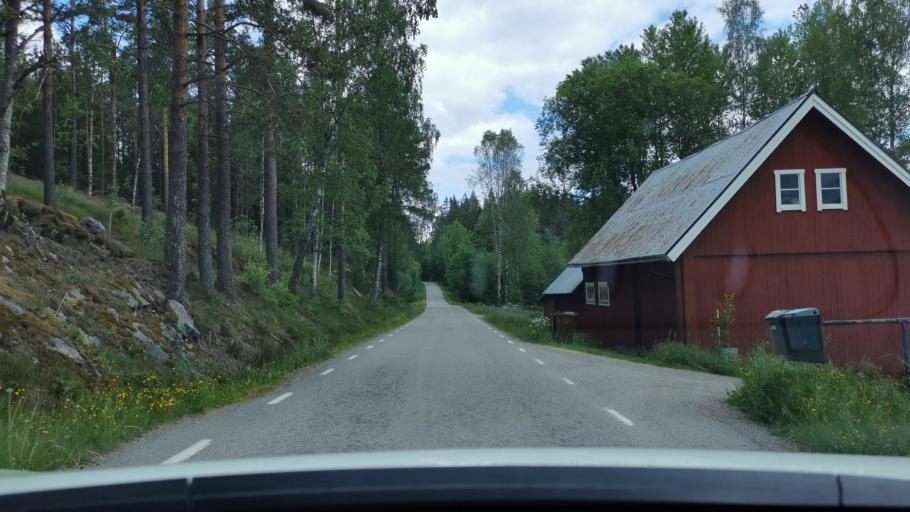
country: SE
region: Vaestra Goetaland
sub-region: Bengtsfors Kommun
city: Dals Langed
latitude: 58.8482
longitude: 12.3326
